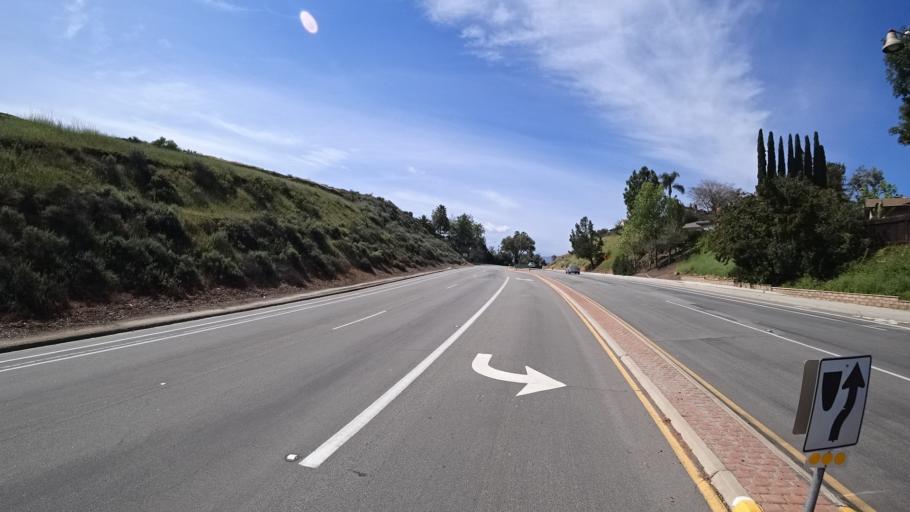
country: US
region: California
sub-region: Ventura County
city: Moorpark
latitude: 34.2341
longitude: -118.8581
